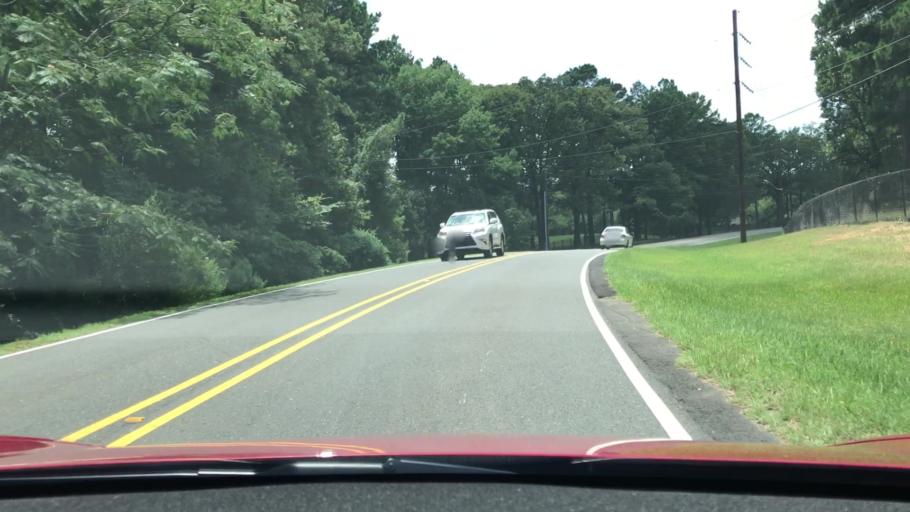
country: US
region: Louisiana
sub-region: De Soto Parish
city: Stonewall
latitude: 32.3666
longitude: -93.6976
